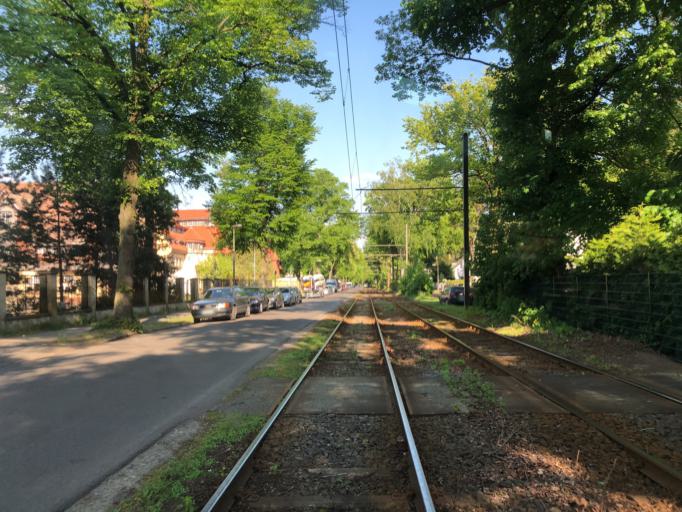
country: DE
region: Berlin
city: Grunau
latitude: 52.4109
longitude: 13.5915
